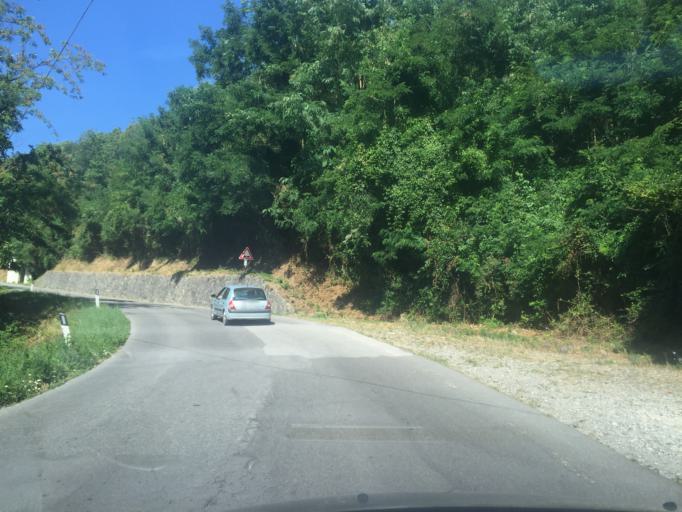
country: IT
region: Tuscany
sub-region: Provincia di Lucca
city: Careggine
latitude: 44.1329
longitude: 10.3128
